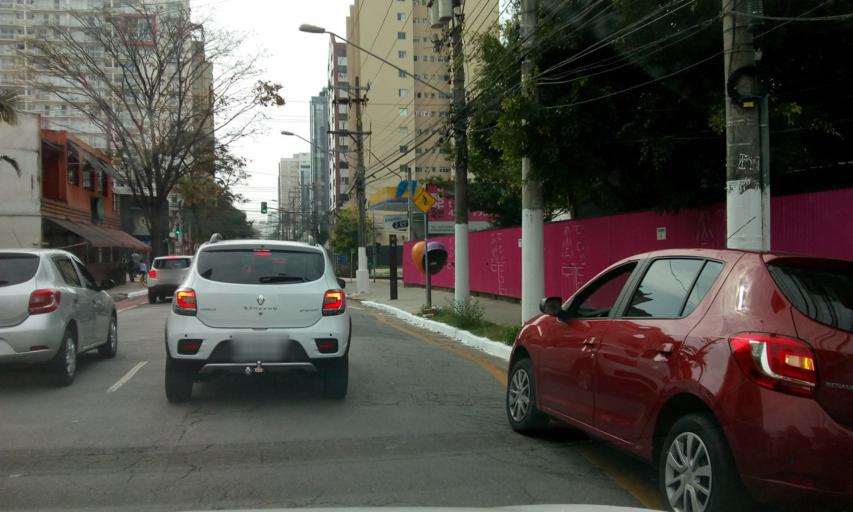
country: BR
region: Sao Paulo
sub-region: Sao Paulo
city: Sao Paulo
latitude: -23.6098
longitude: -46.6641
